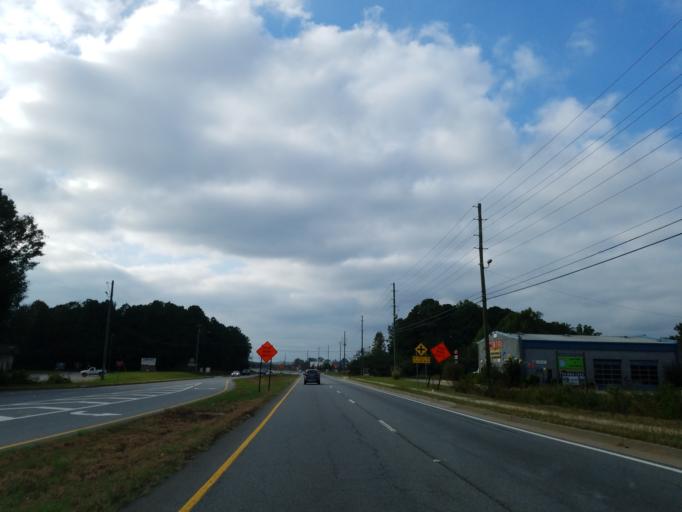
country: US
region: Georgia
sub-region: Cobb County
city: Acworth
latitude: 34.0960
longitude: -84.6243
